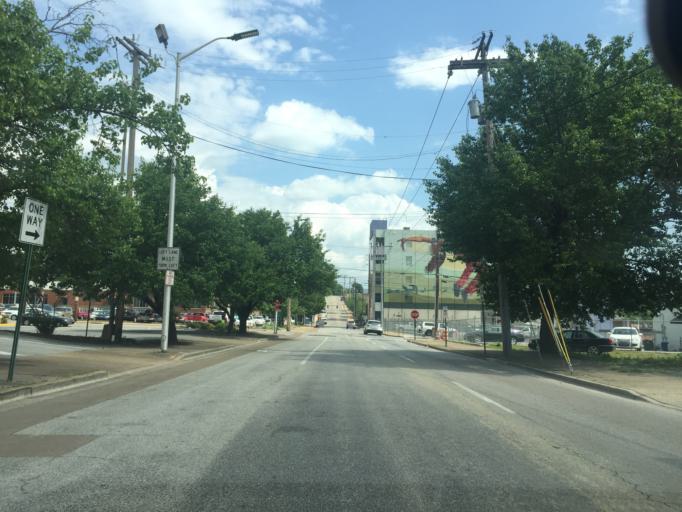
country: US
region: Tennessee
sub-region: Hamilton County
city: Chattanooga
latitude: 35.0432
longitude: -85.3064
